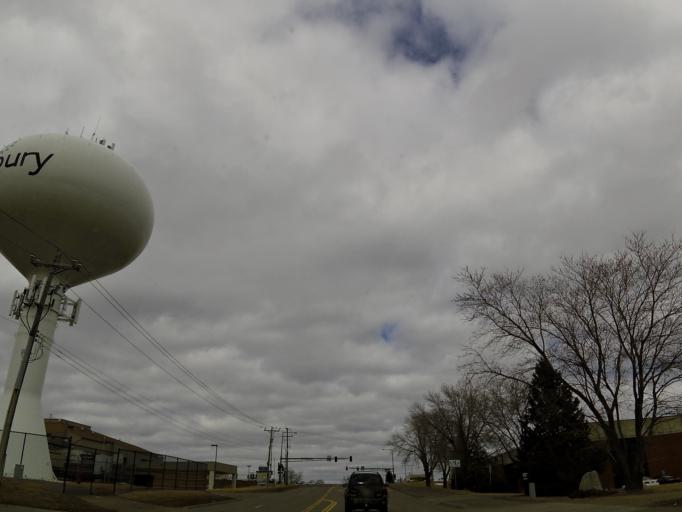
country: US
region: Minnesota
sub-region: Washington County
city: Woodbury
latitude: 44.9238
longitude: -92.9663
